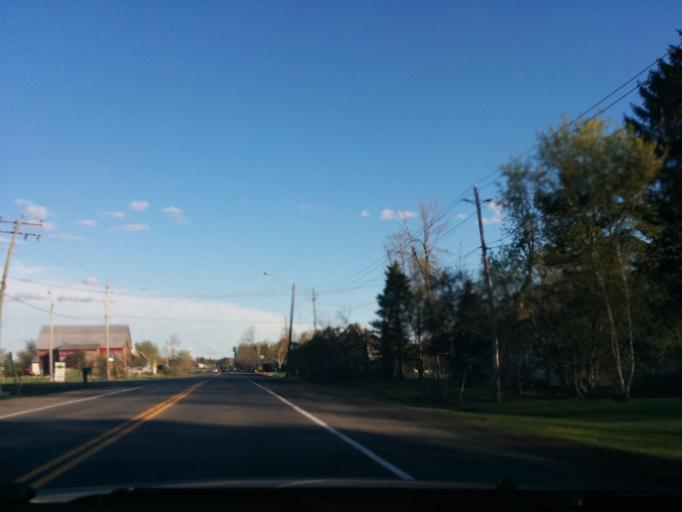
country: CA
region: Ontario
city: Bells Corners
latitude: 45.2490
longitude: -75.6947
